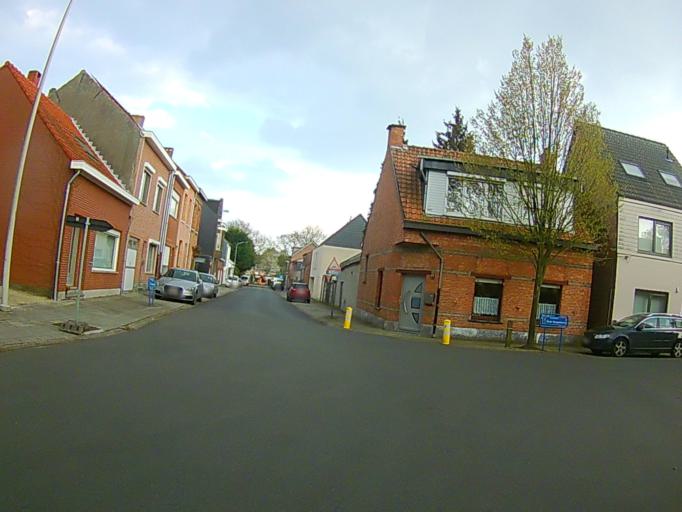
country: BE
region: Flanders
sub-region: Provincie Antwerpen
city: Kapellen
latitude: 51.3085
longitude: 4.4383
